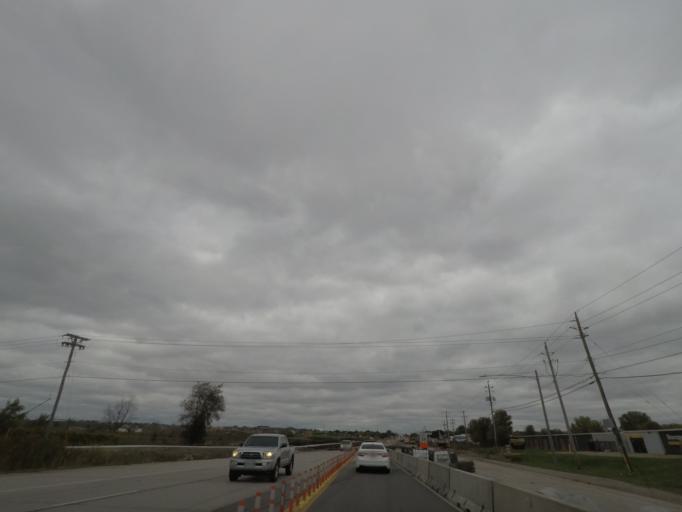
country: US
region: Iowa
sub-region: Polk County
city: Ankeny
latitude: 41.7098
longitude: -93.6005
